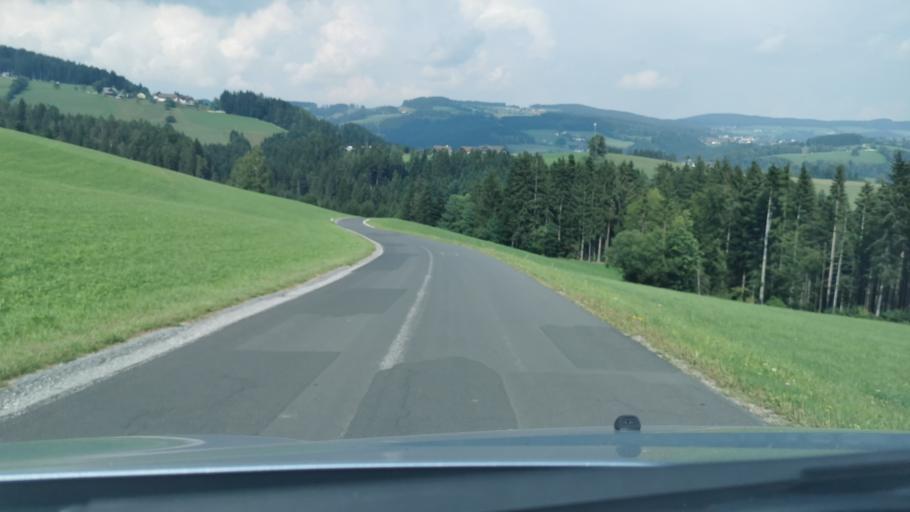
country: AT
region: Styria
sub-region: Politischer Bezirk Weiz
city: Strallegg
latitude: 47.3962
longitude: 15.6844
